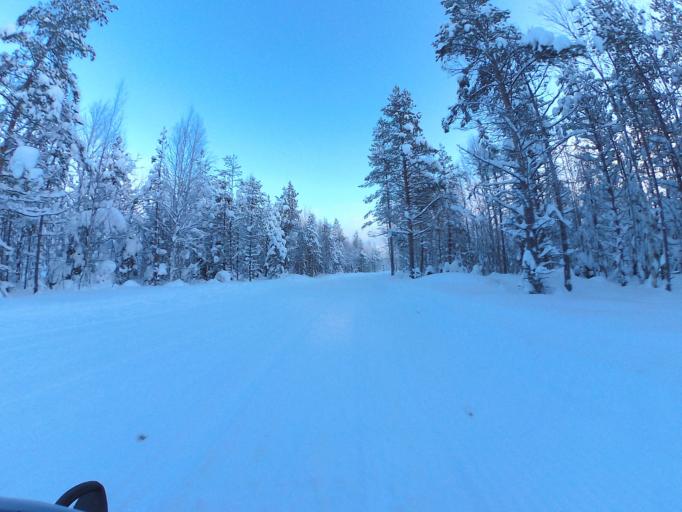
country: FI
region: Lapland
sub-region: Rovaniemi
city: Rovaniemi
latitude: 66.5163
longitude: 25.9996
